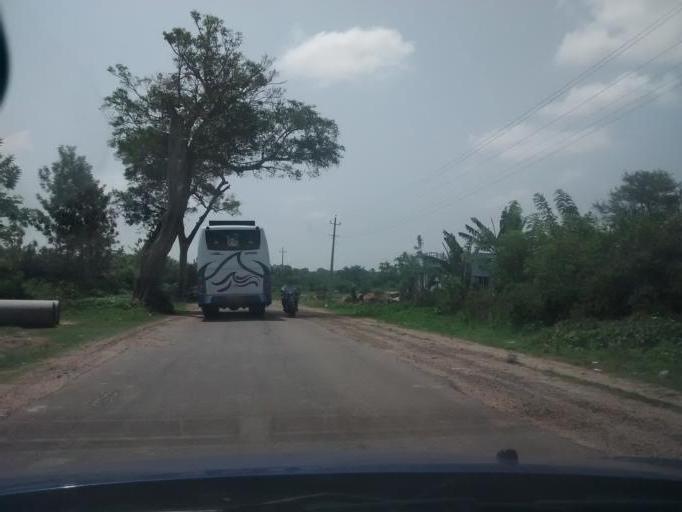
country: IN
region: Karnataka
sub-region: Hassan
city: Konanur
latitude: 12.5819
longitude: 76.1792
